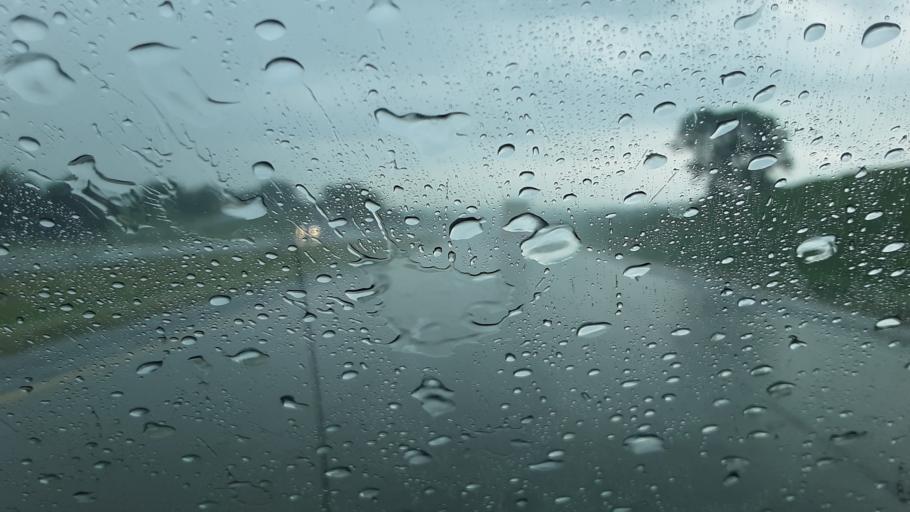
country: US
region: Iowa
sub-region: Pottawattamie County
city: Council Bluffs
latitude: 41.2847
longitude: -95.7815
